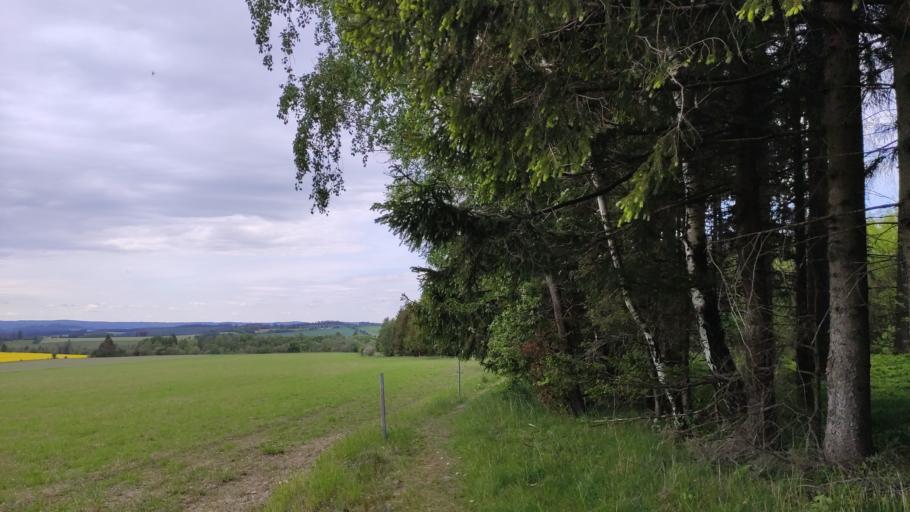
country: DE
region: Bavaria
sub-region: Upper Franconia
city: Reichenbach
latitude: 50.4645
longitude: 11.4532
